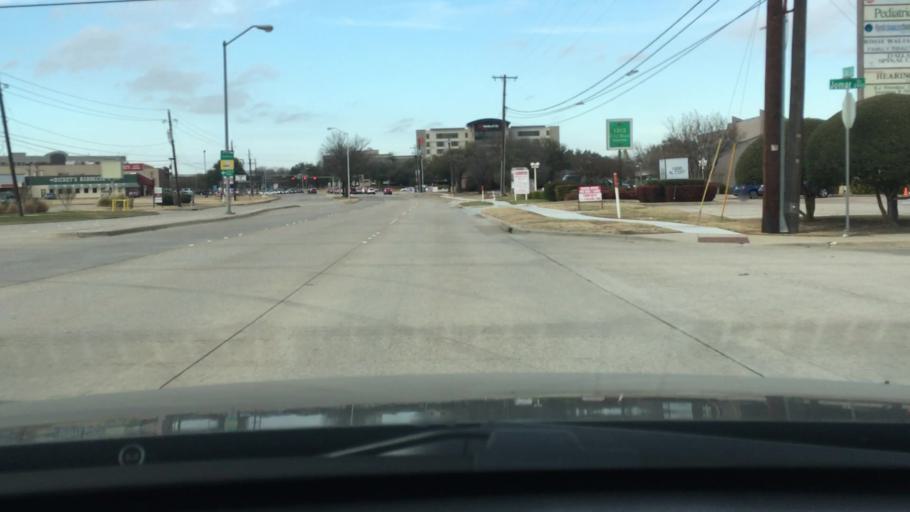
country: US
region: Texas
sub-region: Collin County
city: Plano
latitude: 33.0162
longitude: -96.7666
